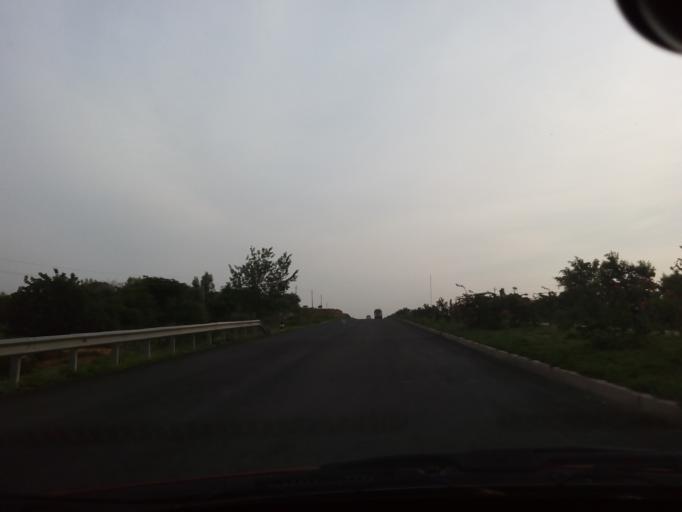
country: IN
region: Karnataka
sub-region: Chikkaballapur
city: Gudibanda
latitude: 13.6051
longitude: 77.7873
